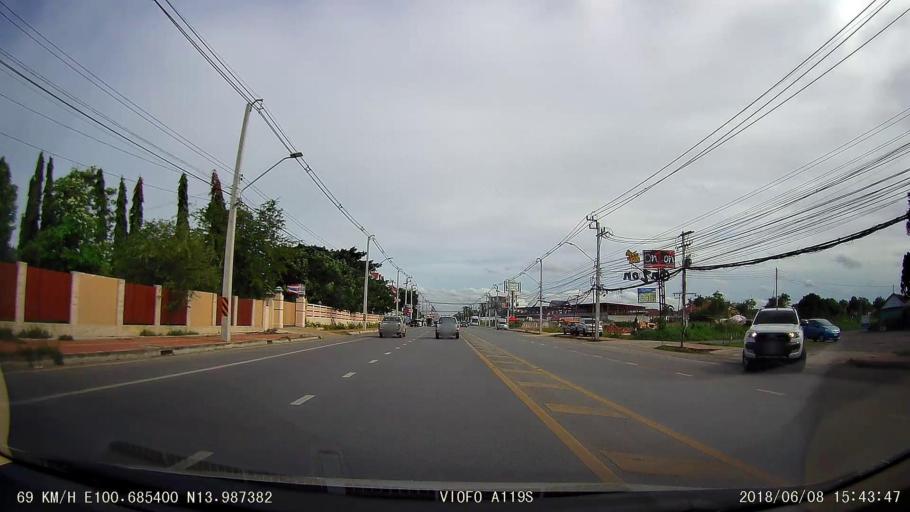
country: TH
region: Pathum Thani
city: Thanyaburi
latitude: 13.9872
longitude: 100.6854
